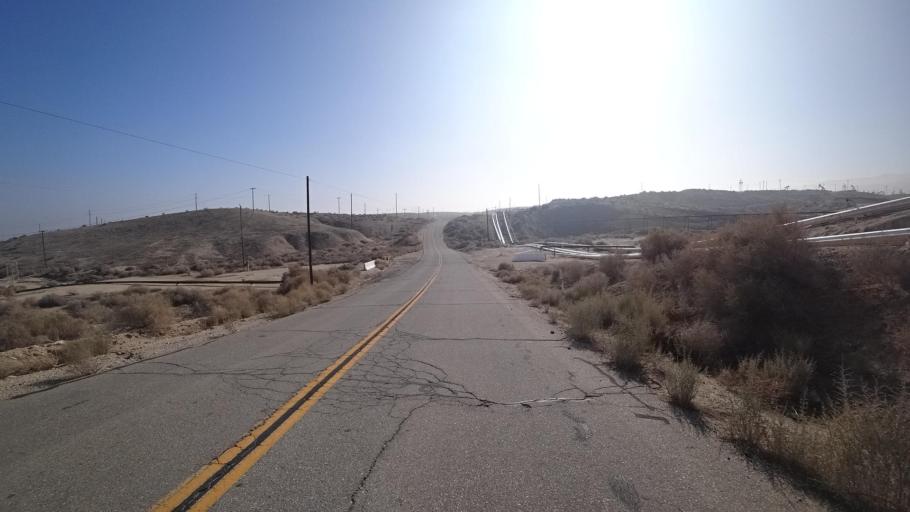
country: US
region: California
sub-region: Kern County
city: Taft Heights
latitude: 35.1538
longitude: -119.5198
